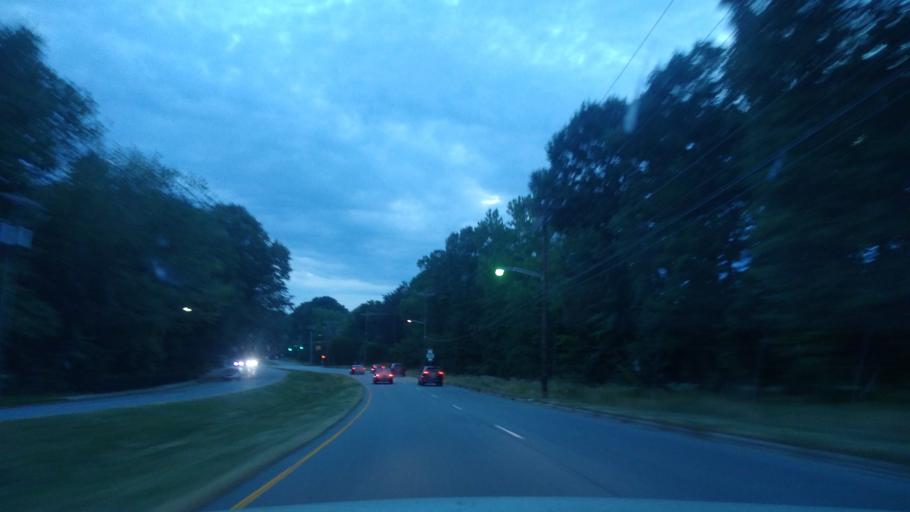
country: US
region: North Carolina
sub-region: Guilford County
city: Greensboro
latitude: 36.1104
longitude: -79.7889
